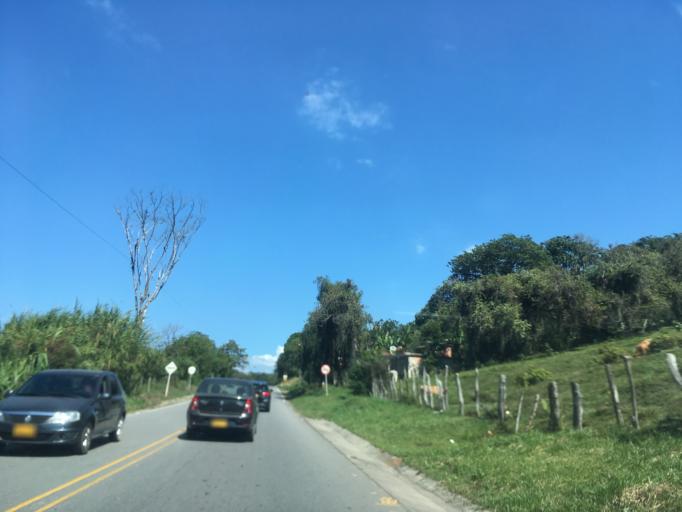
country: CO
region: Santander
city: Suaita
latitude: 6.0784
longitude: -73.3977
